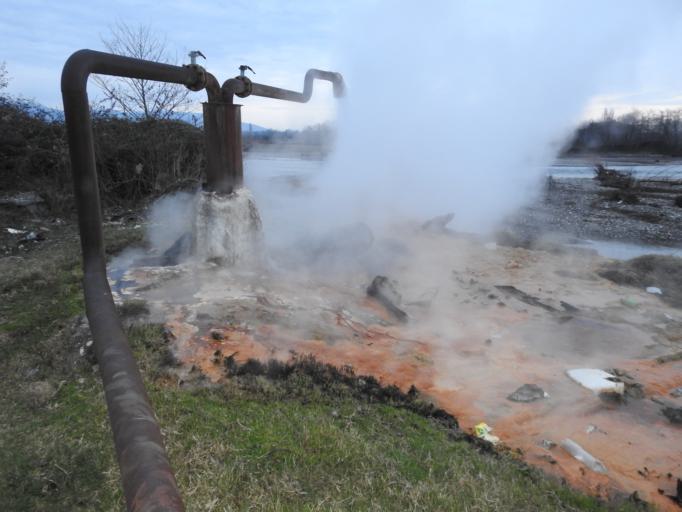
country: GE
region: Abkhazia
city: Och'amch'ire
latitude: 42.7036
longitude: 41.4767
